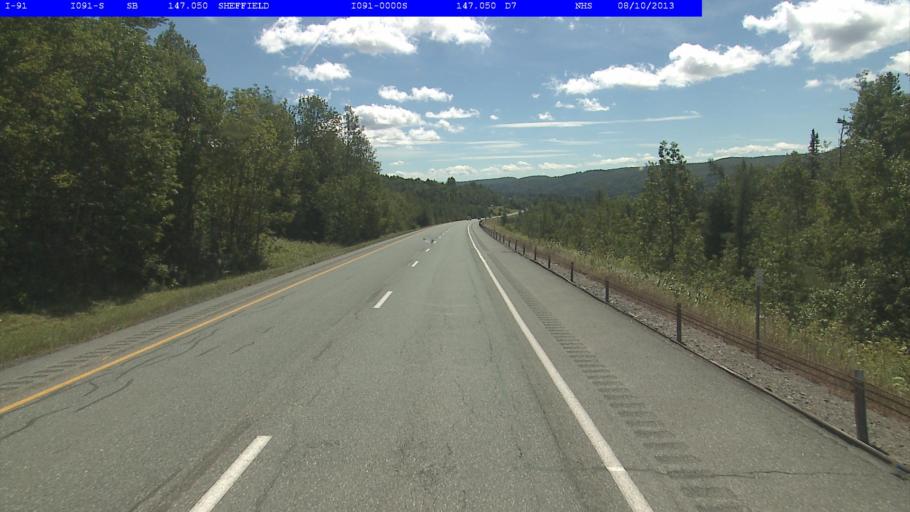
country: US
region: Vermont
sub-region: Caledonia County
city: Lyndonville
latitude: 44.6229
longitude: -72.1254
